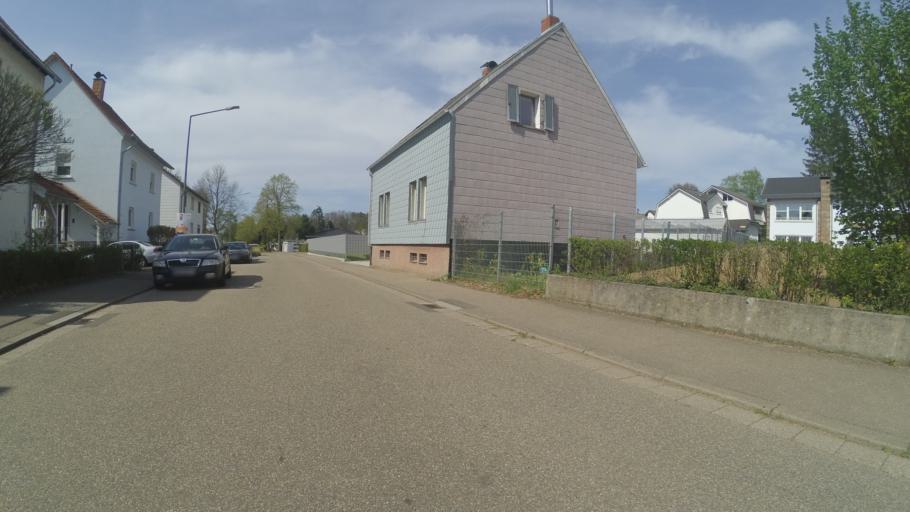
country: DE
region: Saarland
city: Homburg
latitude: 49.3398
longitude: 7.3640
